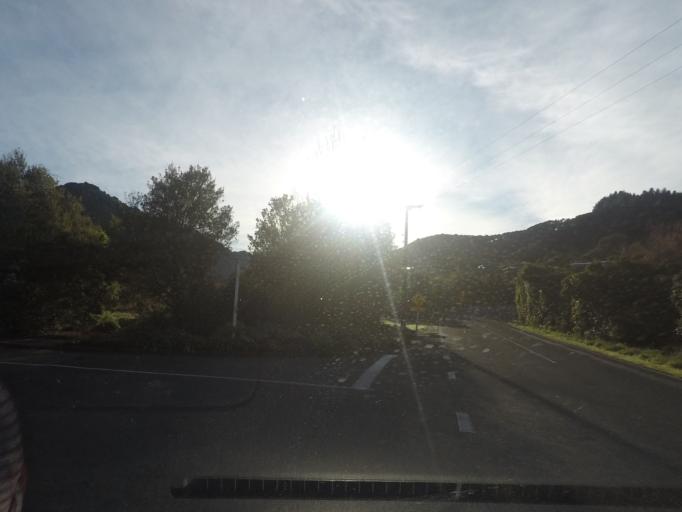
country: NZ
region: Tasman
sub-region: Tasman District
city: Takaka
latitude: -40.8117
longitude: 172.9170
